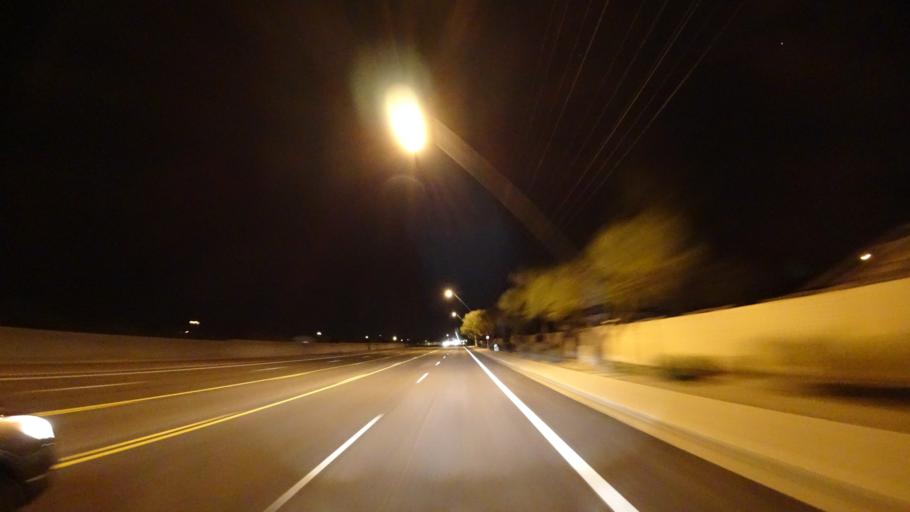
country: US
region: Arizona
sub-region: Pinal County
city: Apache Junction
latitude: 33.3933
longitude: -111.6625
